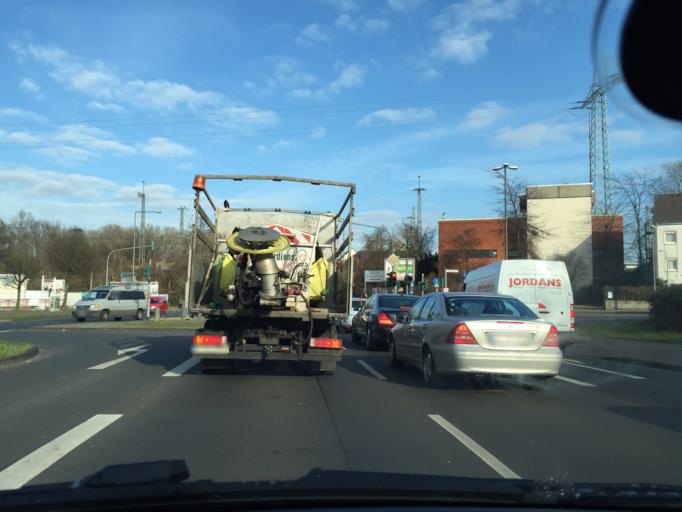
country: DE
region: North Rhine-Westphalia
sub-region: Regierungsbezirk Koln
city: Neustadt/Sued
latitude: 50.9166
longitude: 6.9484
